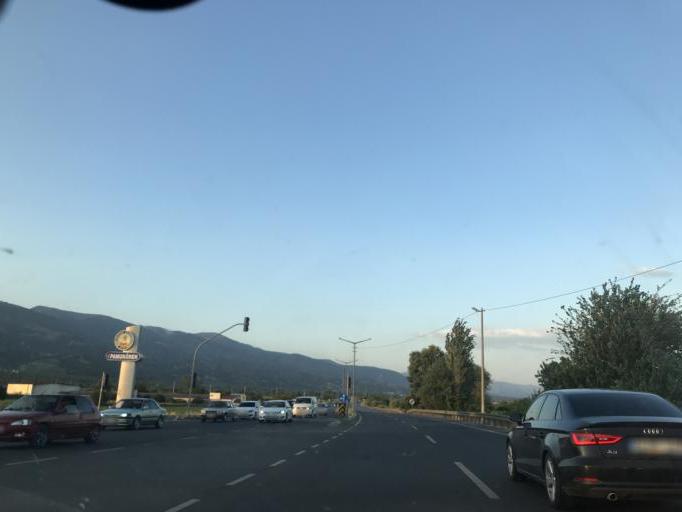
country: TR
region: Aydin
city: Pamukoren
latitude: 37.9063
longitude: 28.5567
